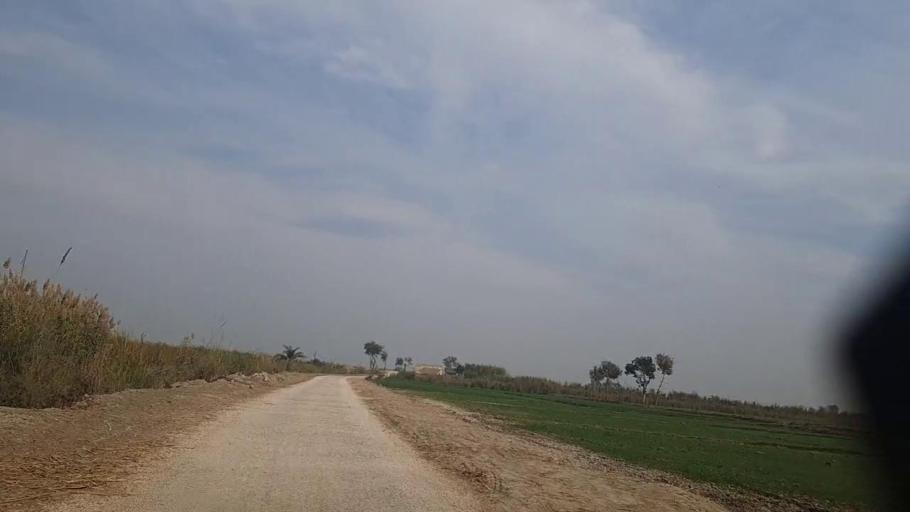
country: PK
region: Sindh
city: Daur
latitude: 26.3767
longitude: 68.2563
